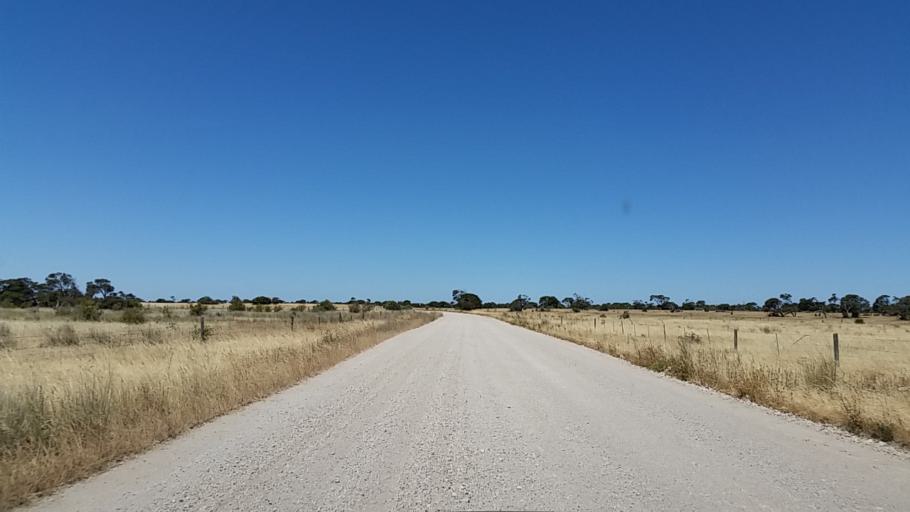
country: AU
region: South Australia
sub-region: Yorke Peninsula
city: Honiton
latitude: -35.0802
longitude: 137.4845
